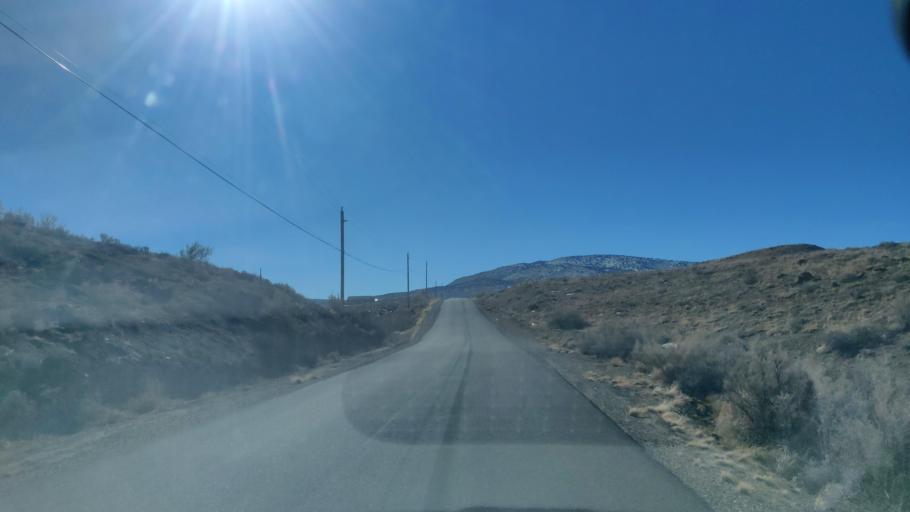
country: US
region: Colorado
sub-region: Mesa County
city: Palisade
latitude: 39.0953
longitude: -108.3296
